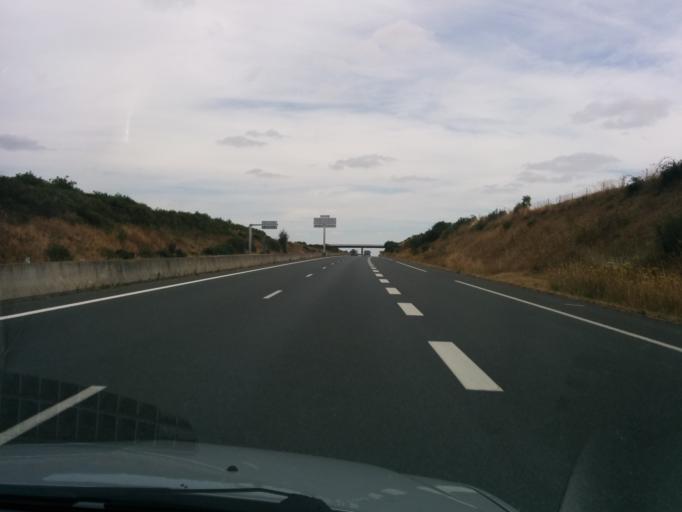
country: FR
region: Poitou-Charentes
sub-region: Departement des Deux-Sevres
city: Saint-Pierre-des-Echaubrognes
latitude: 46.9287
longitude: -0.7228
